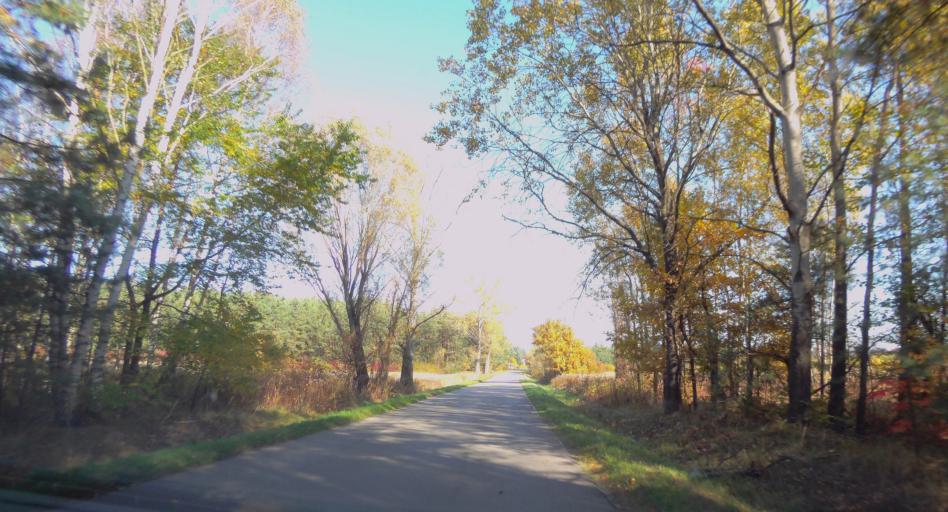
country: PL
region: Subcarpathian Voivodeship
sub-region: Powiat lezajski
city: Wola Zarczycka
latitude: 50.2595
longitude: 22.2391
